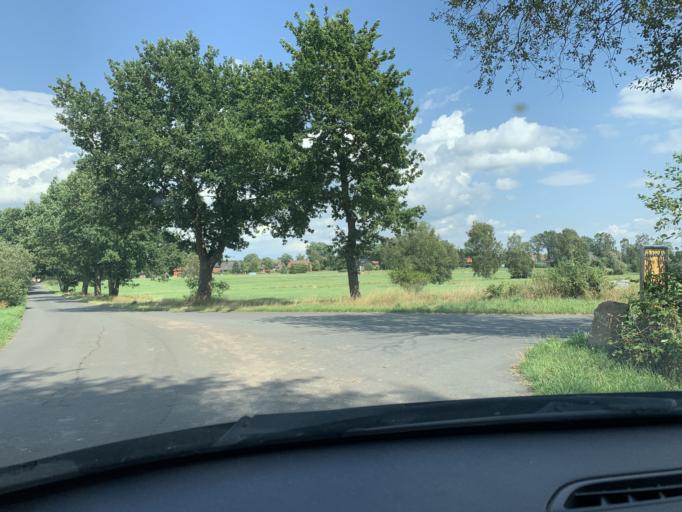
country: DE
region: Lower Saxony
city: Undeloh
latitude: 53.2244
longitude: 9.9156
